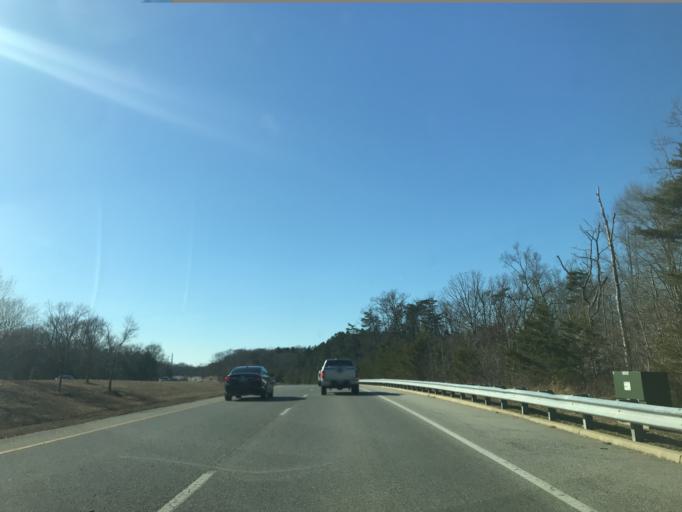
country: US
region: Maryland
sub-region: Charles County
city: Saint Charles
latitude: 38.5604
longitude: -76.9395
